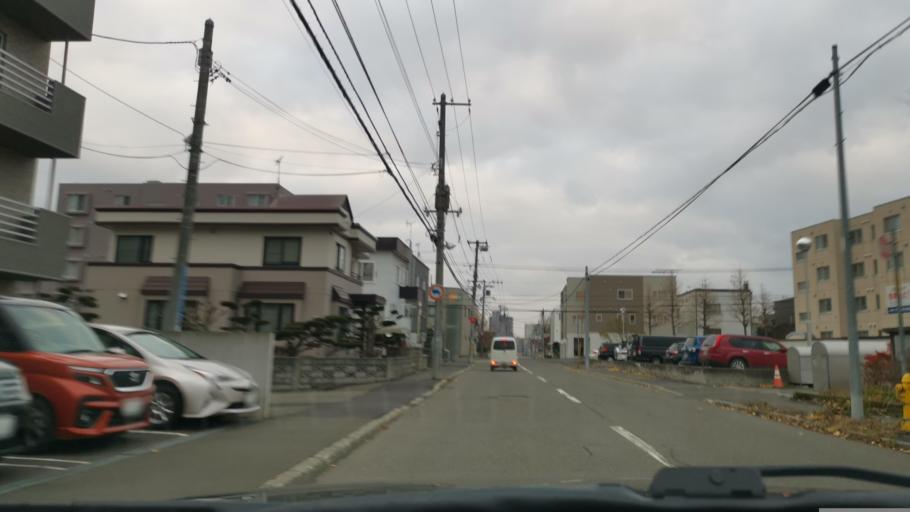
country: JP
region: Hokkaido
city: Sapporo
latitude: 43.0395
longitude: 141.4161
